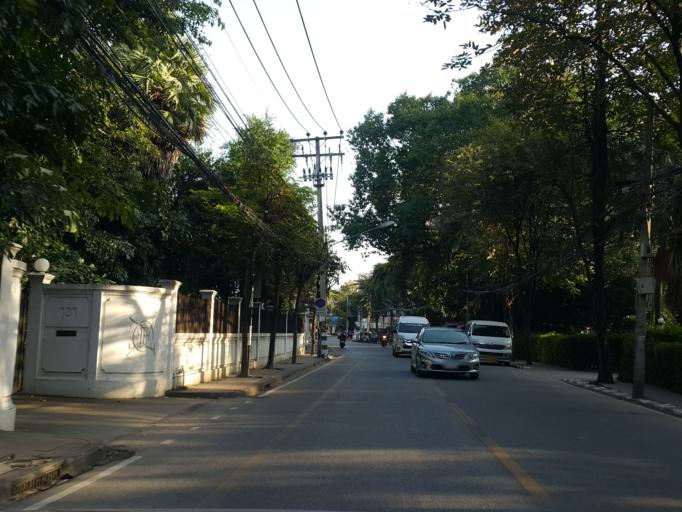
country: TH
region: Chiang Mai
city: Chiang Mai
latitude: 18.7812
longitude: 99.0037
